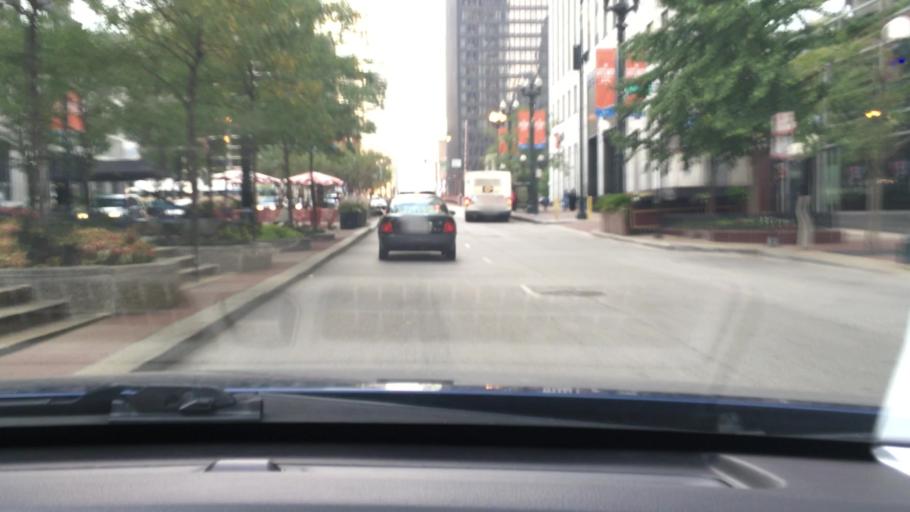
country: US
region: Illinois
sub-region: Cook County
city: Chicago
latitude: 41.8859
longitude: -87.6279
